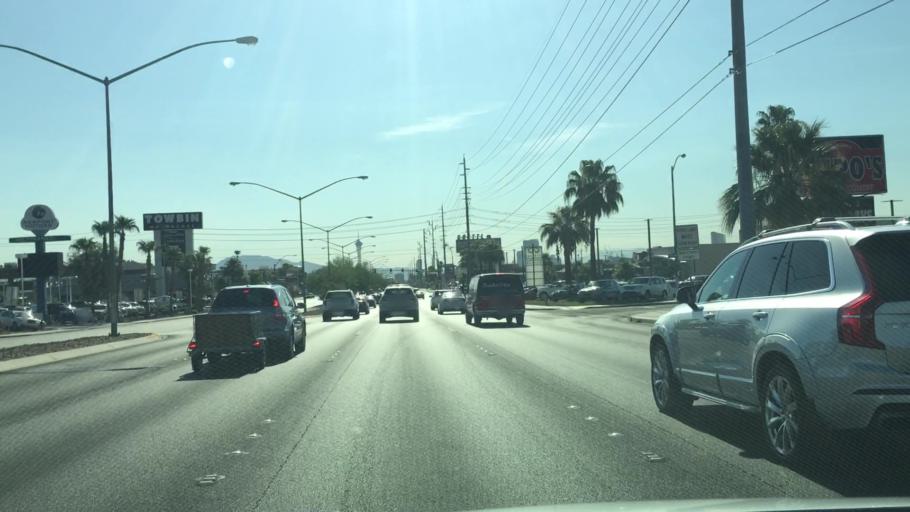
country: US
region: Nevada
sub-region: Clark County
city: Spring Valley
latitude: 36.1443
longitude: -115.2194
